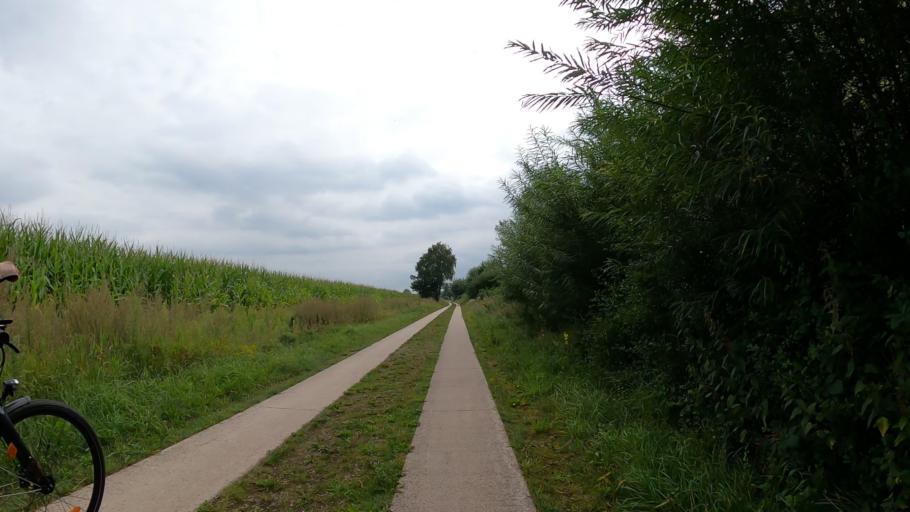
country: DE
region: Lower Saxony
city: Stelle
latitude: 53.3664
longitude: 10.1556
